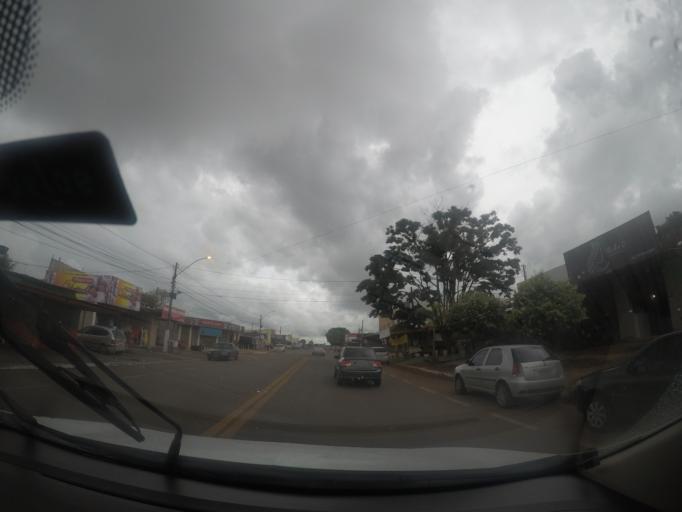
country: BR
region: Goias
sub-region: Trindade
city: Trindade
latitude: -16.6369
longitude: -49.3903
